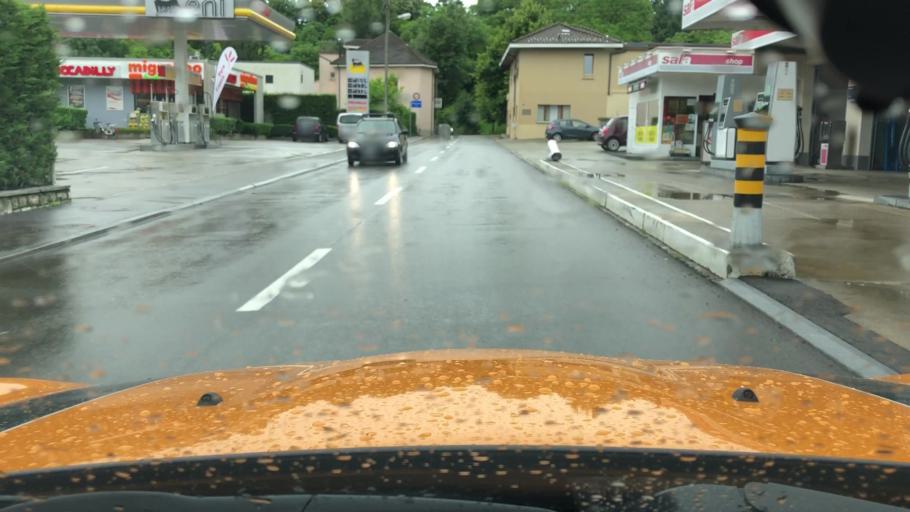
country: CH
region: Ticino
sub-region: Mendrisio District
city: Novazzano
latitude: 45.8379
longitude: 8.9827
